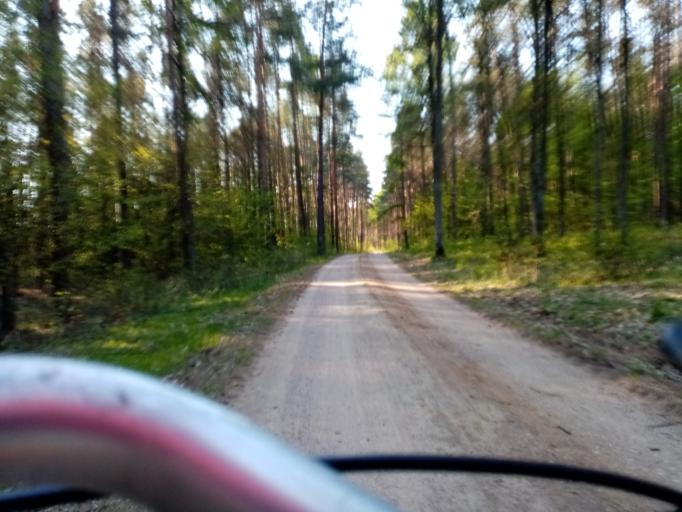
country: PL
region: Kujawsko-Pomorskie
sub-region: Powiat brodnicki
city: Gorzno
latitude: 53.1663
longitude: 19.6754
